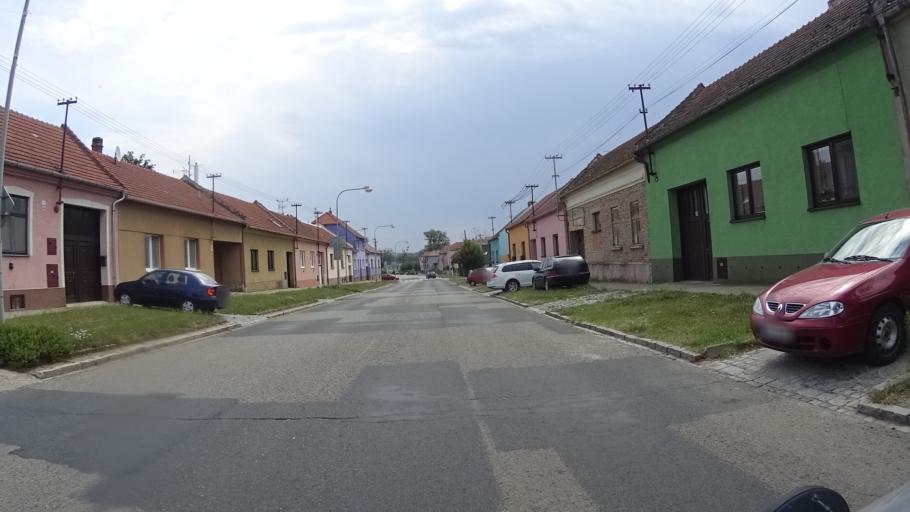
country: CZ
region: South Moravian
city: Podivin
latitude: 48.8292
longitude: 16.8532
